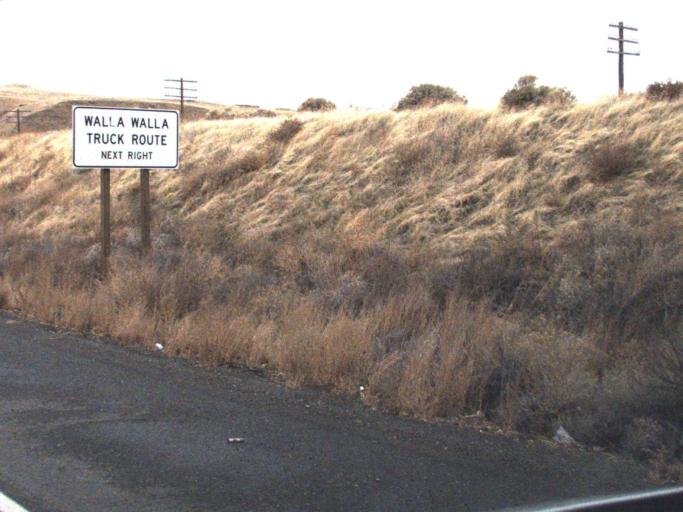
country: US
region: Washington
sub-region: Benton County
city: Finley
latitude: 46.0660
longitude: -118.9080
